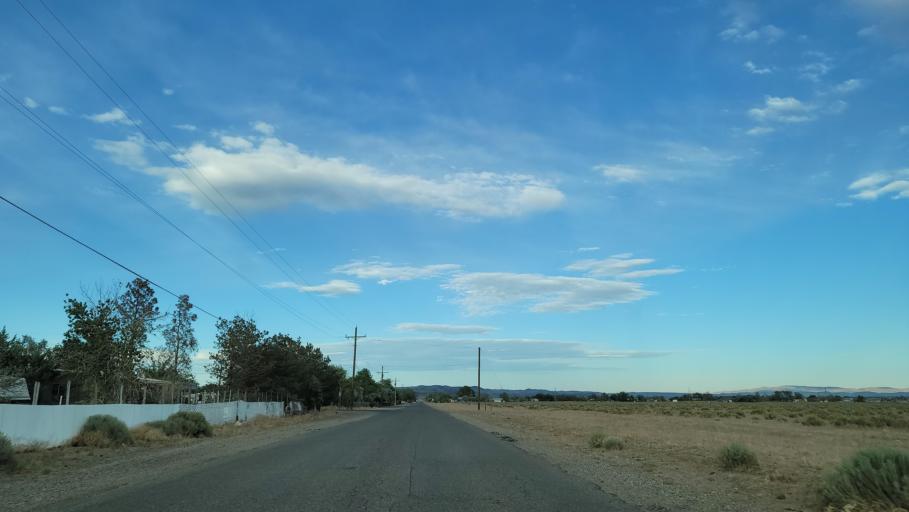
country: US
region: Nevada
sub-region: Lyon County
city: Silver Springs
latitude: 39.3899
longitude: -119.2463
